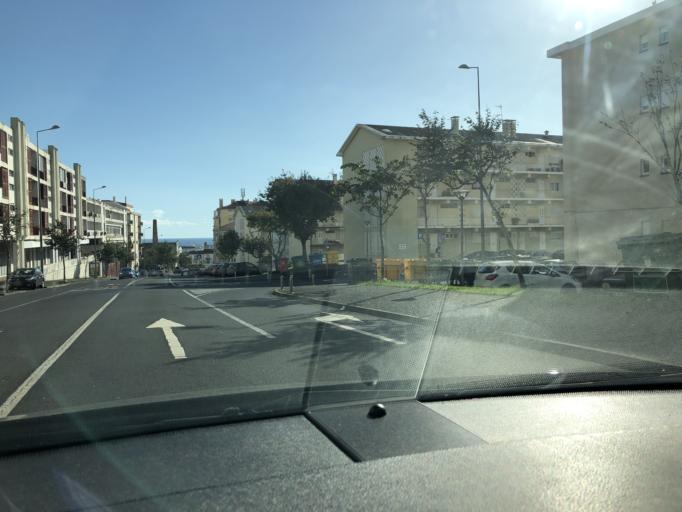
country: PT
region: Azores
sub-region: Ponta Delgada
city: Rosto de Cao
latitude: 37.7454
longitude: -25.6568
